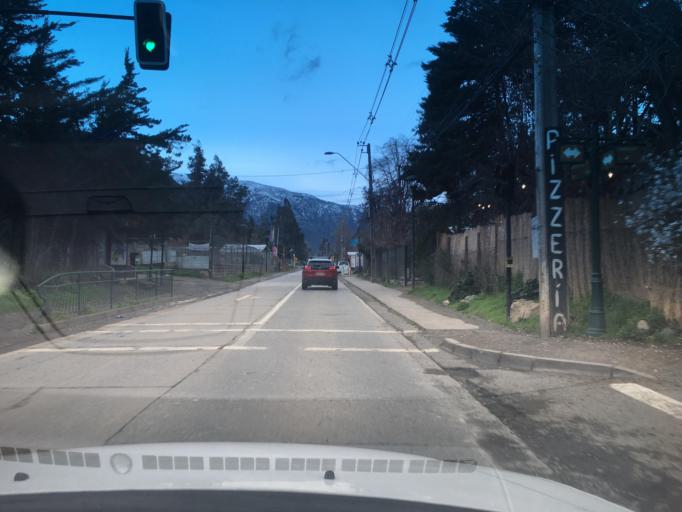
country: CL
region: Santiago Metropolitan
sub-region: Provincia de Cordillera
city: Puente Alto
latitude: -33.5845
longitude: -70.3958
